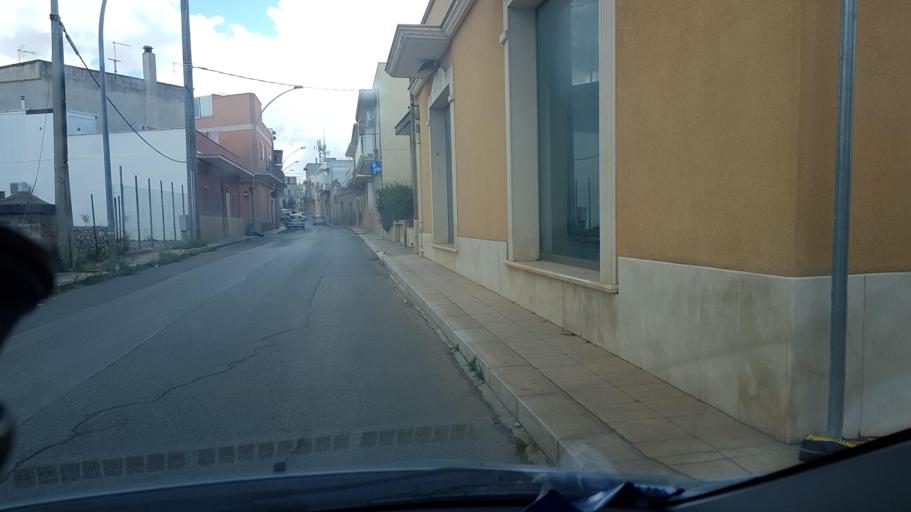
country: IT
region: Apulia
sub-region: Provincia di Brindisi
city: San Vito dei Normanni
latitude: 40.6592
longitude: 17.7120
